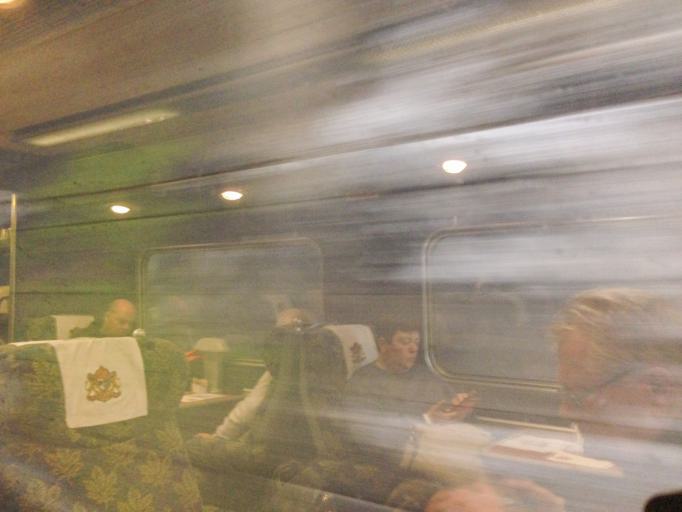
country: GB
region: Scotland
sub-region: Highland
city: Fort William
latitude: 56.8231
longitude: -5.0938
